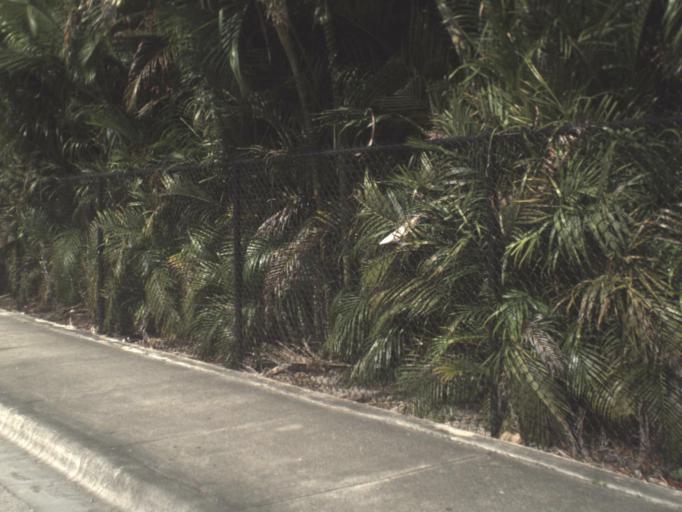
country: US
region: Florida
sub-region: Miami-Dade County
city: Doral
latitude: 25.8111
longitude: -80.3443
